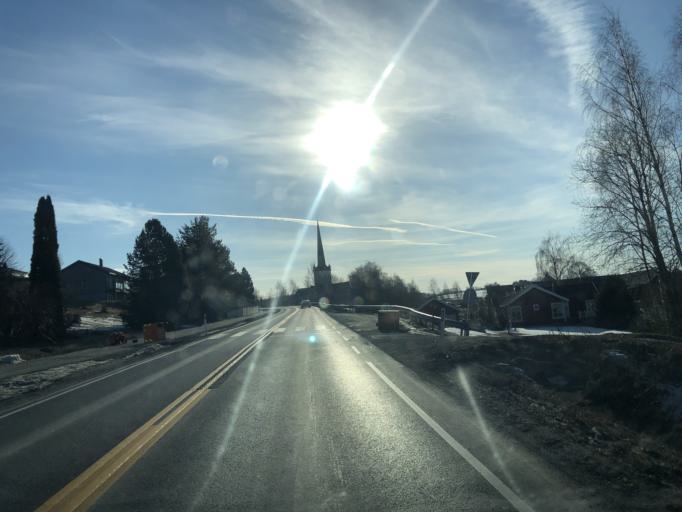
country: NO
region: Hedmark
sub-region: Ringsaker
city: Moelv
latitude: 60.9044
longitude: 10.7189
